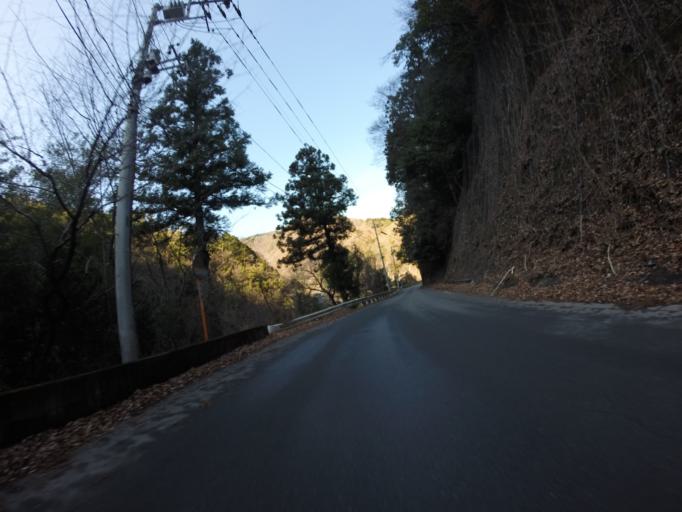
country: JP
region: Yamanashi
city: Ryuo
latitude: 35.4110
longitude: 138.3553
